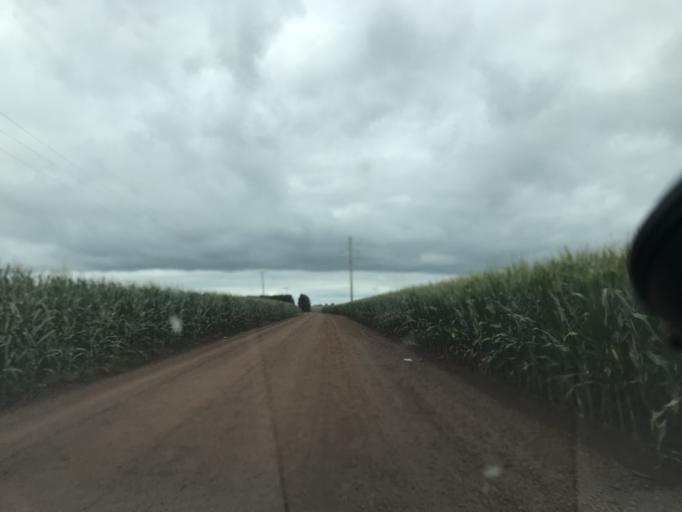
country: BR
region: Parana
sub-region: Palotina
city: Palotina
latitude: -24.2958
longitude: -53.8178
